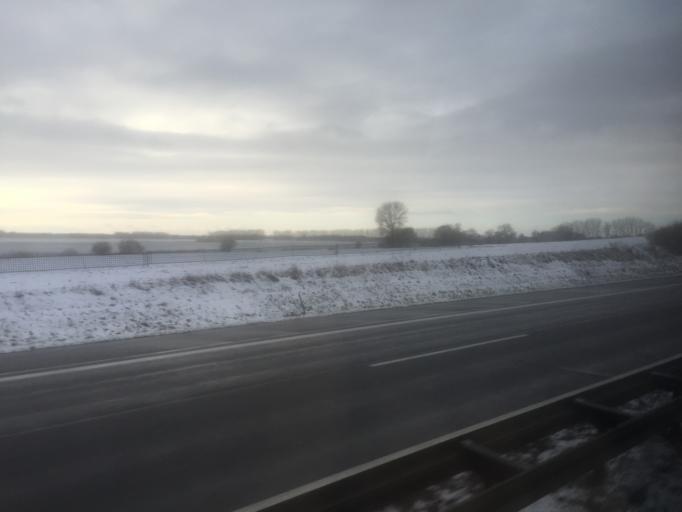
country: DE
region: Brandenburg
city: Kremmen
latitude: 52.7452
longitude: 12.8969
